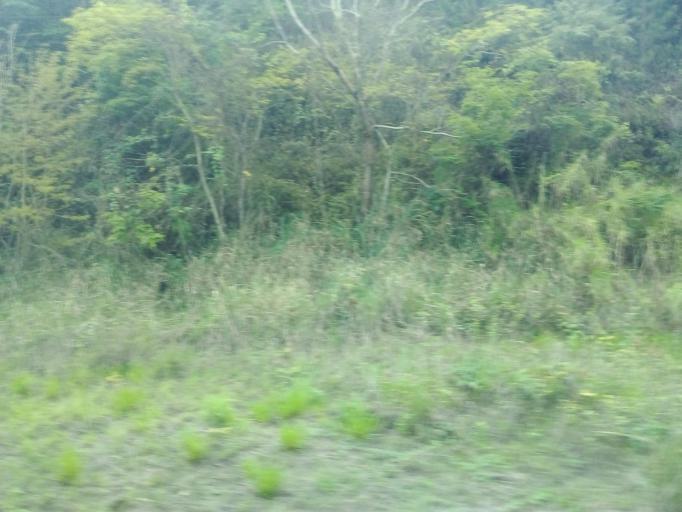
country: BR
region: Minas Gerais
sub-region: Nova Era
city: Nova Era
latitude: -19.7288
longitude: -42.9841
